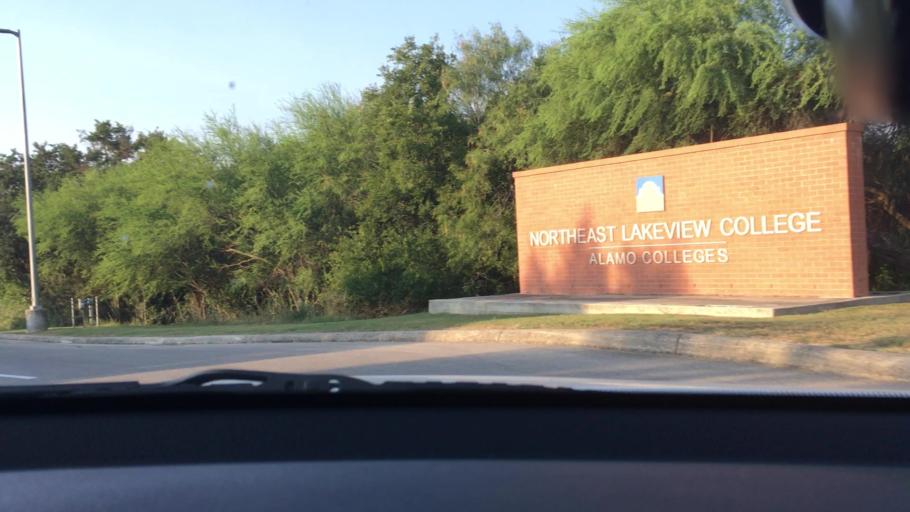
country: US
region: Texas
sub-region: Bexar County
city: Live Oak
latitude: 29.5524
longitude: -98.3261
